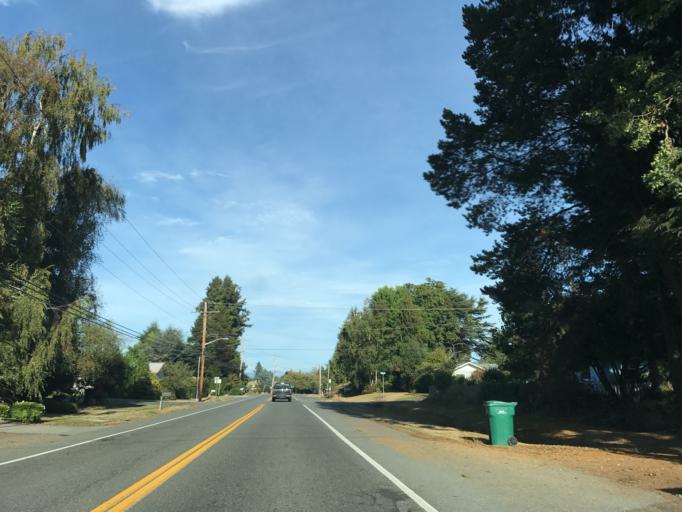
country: US
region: Washington
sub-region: Skagit County
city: Anacortes
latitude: 48.5121
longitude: -122.6386
